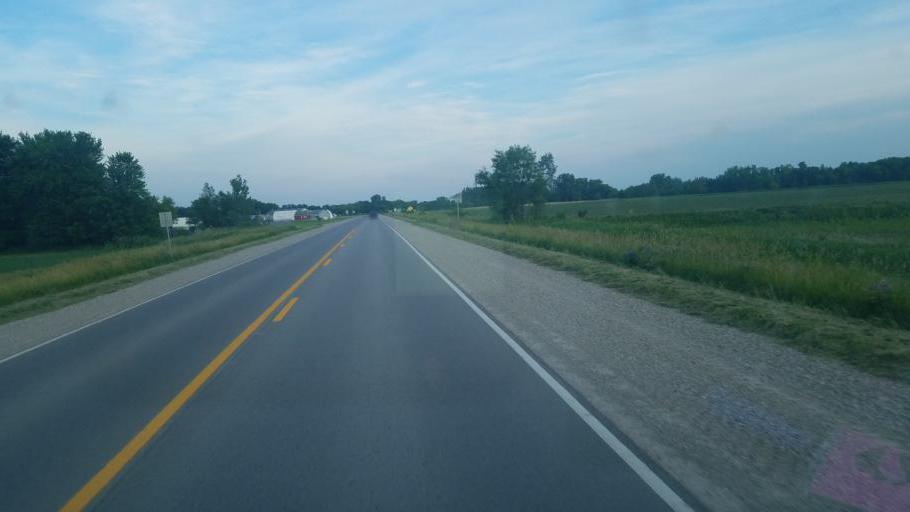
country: US
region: Iowa
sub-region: Benton County
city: Belle Plaine
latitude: 41.9037
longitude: -92.2943
